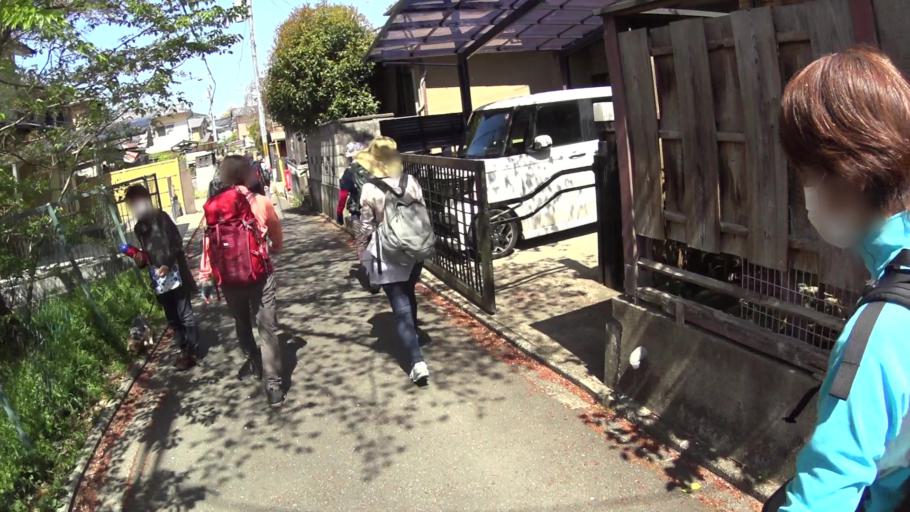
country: JP
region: Kyoto
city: Kyoto
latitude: 34.9831
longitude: 135.7775
